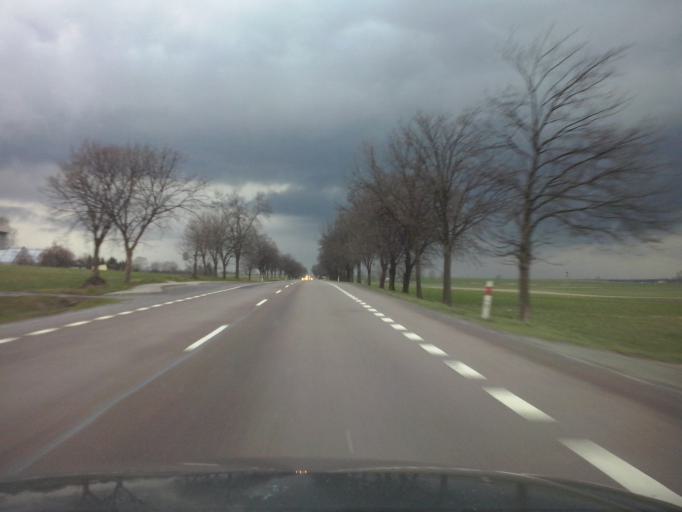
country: PL
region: Lublin Voivodeship
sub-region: Powiat chelmski
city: Rejowiec Fabryczny
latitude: 51.1768
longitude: 23.2322
